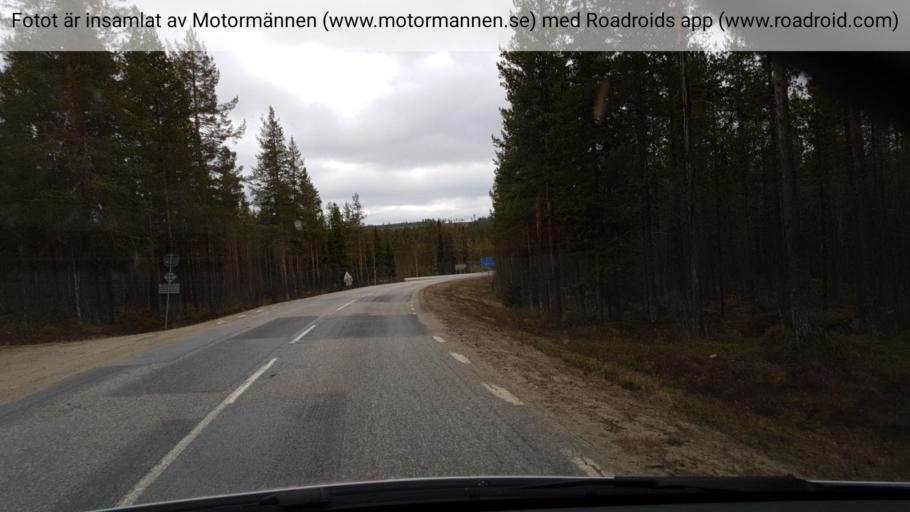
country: SE
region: Vaesternorrland
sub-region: OErnskoeldsviks Kommun
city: Bredbyn
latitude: 63.8869
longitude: 18.5192
